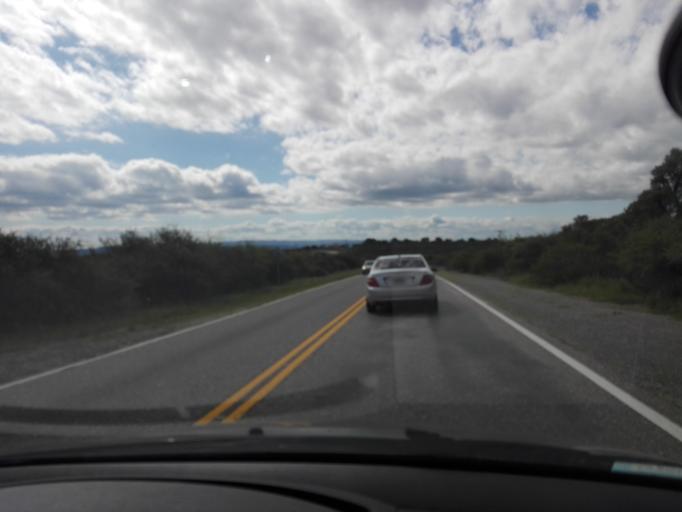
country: AR
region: Cordoba
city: Mina Clavero
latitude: -31.7426
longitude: -64.9365
